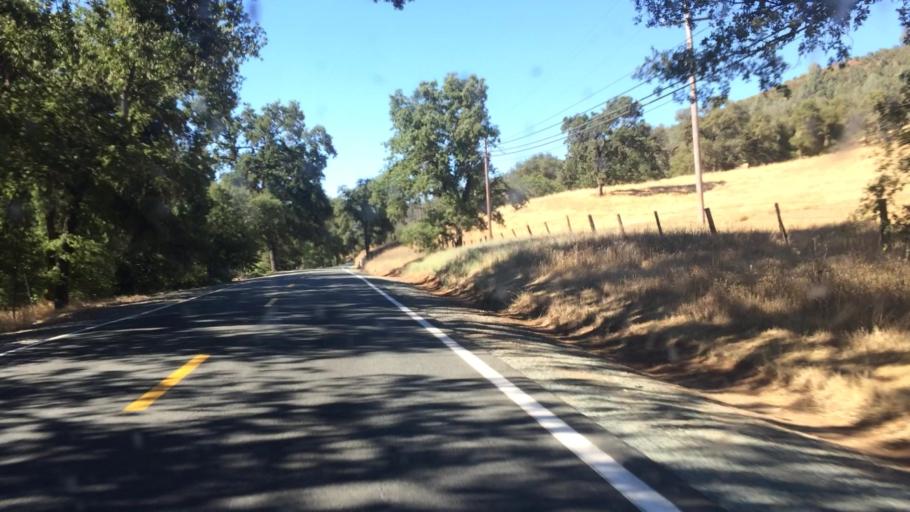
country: US
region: California
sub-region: Amador County
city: Plymouth
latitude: 38.5171
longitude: -120.8484
